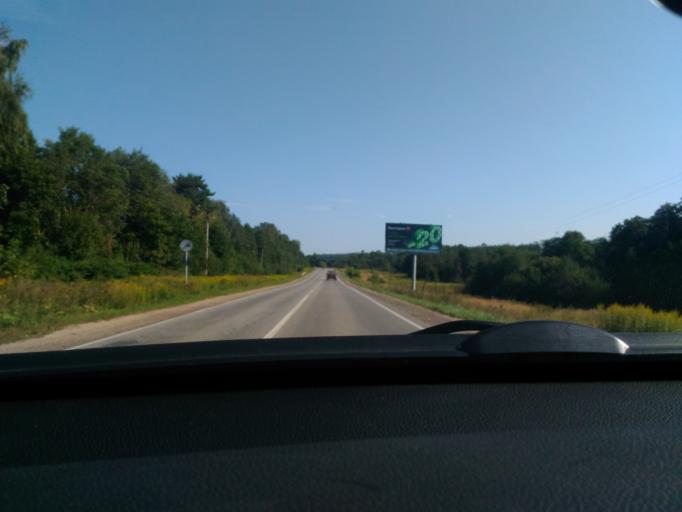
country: RU
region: Moskovskaya
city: Podosinki
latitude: 56.2157
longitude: 37.5454
